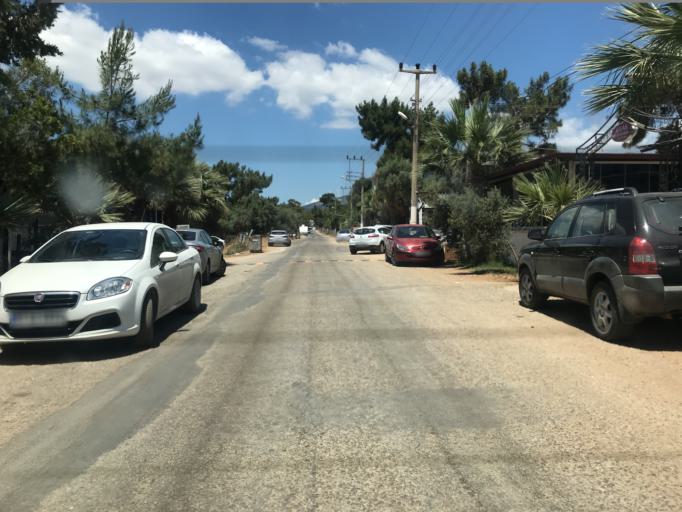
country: TR
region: Aydin
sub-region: Didim
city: Didim
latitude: 37.4059
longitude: 27.4272
